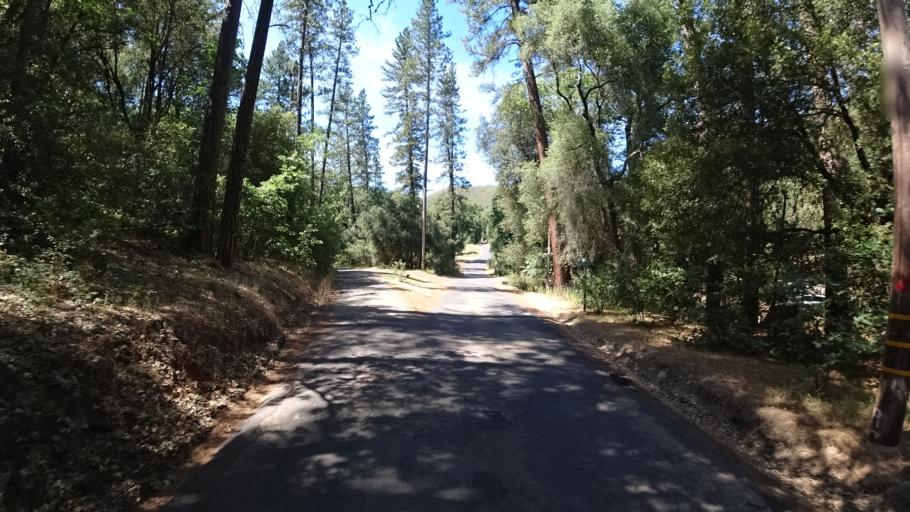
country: US
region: California
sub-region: Calaveras County
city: Murphys
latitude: 38.1564
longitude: -120.4736
